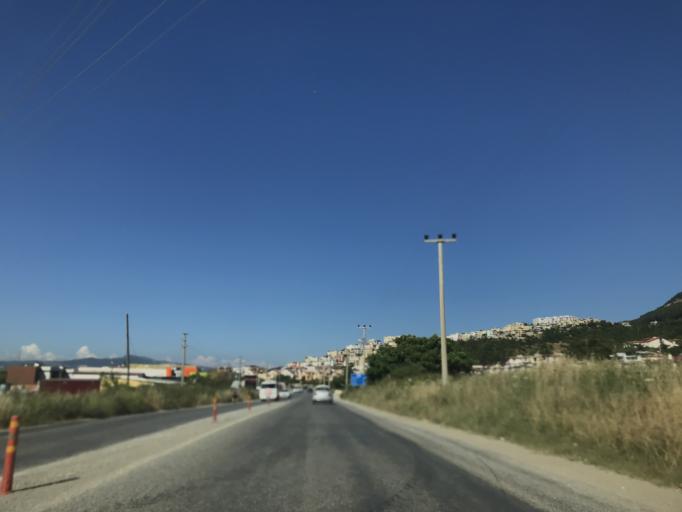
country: TR
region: Aydin
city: Davutlar
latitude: 37.7209
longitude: 27.2513
